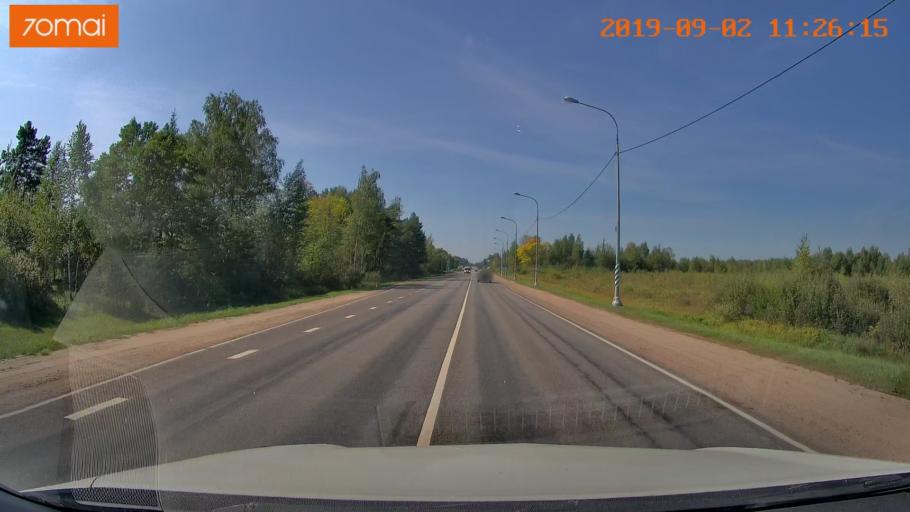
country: RU
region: Smolensk
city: Roslavl'
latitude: 53.9938
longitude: 32.9344
